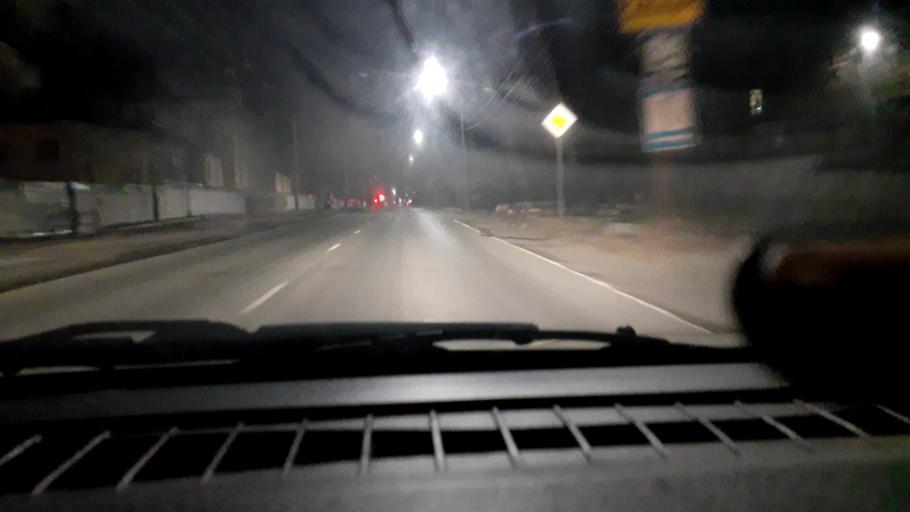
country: RU
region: Nizjnij Novgorod
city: Dzerzhinsk
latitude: 56.2464
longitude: 43.4824
